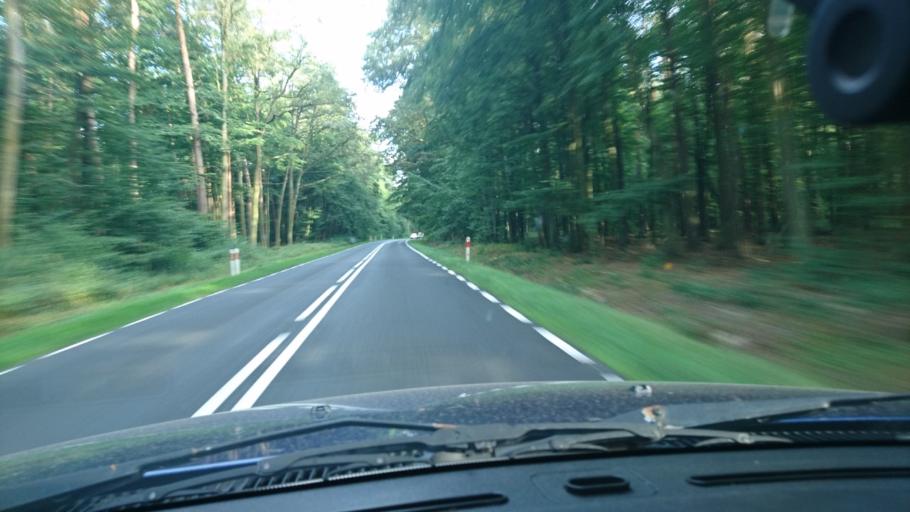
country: PL
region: Greater Poland Voivodeship
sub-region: Powiat krotoszynski
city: Krotoszyn
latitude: 51.6576
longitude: 17.4750
